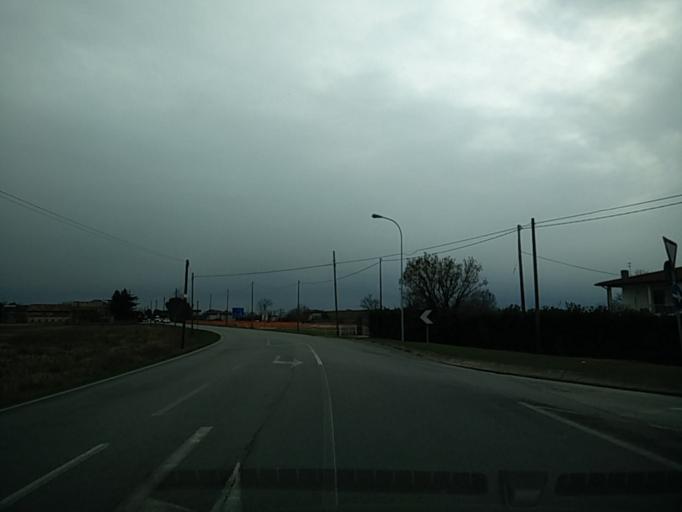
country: IT
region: Veneto
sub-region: Provincia di Treviso
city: Ca' Rainati
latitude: 45.7532
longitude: 11.8646
